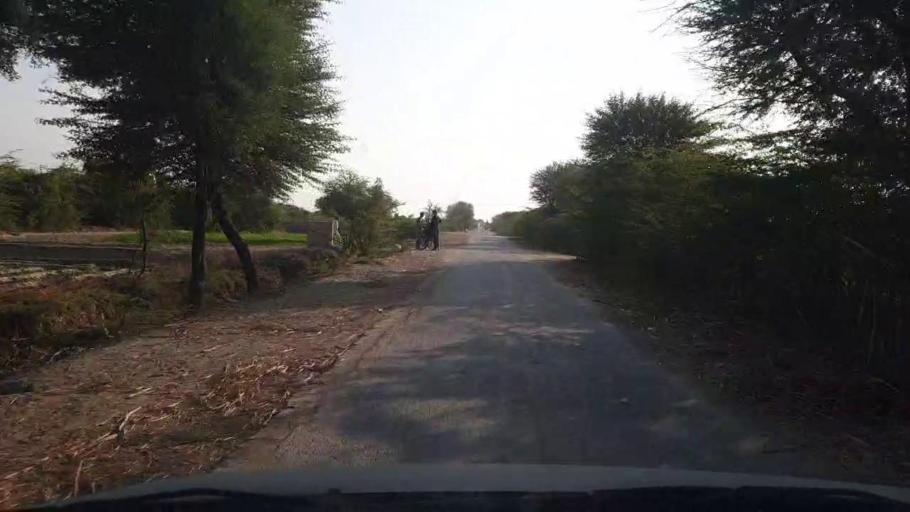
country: PK
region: Sindh
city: Samaro
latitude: 25.2653
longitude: 69.3597
